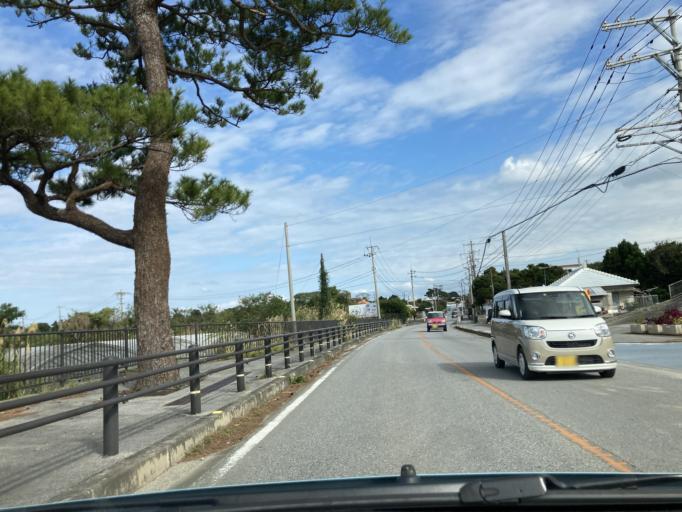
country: JP
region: Okinawa
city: Nago
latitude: 26.6958
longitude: 127.9484
